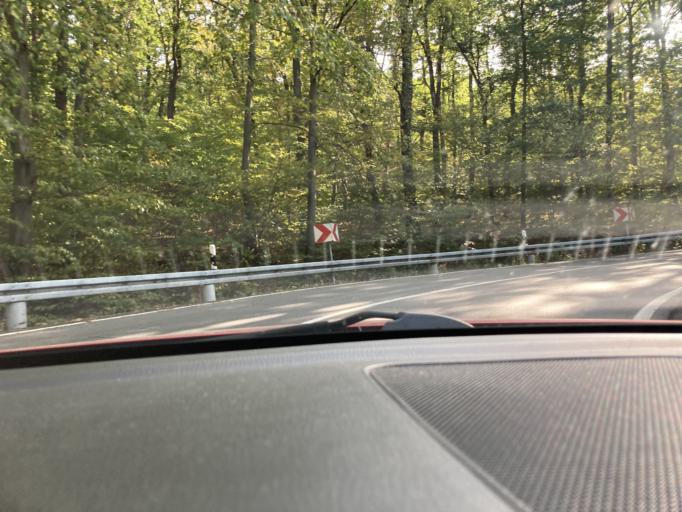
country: DE
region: Saxony-Anhalt
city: Thale
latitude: 51.7407
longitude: 11.0409
